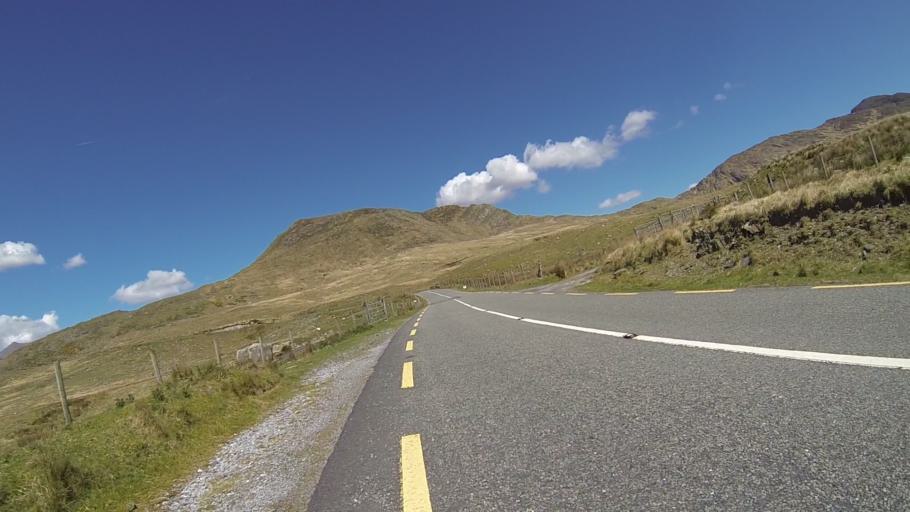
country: IE
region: Munster
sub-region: Ciarrai
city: Kenmare
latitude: 51.9283
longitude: -9.6465
